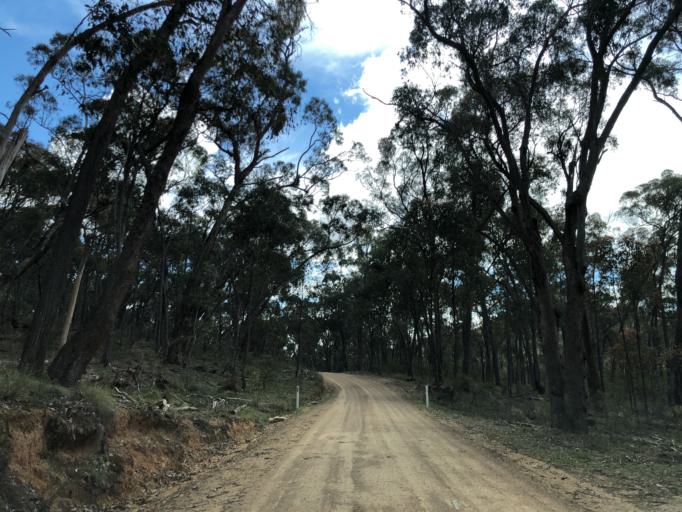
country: AU
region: Victoria
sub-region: Benalla
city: Benalla
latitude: -36.7442
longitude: 146.1577
